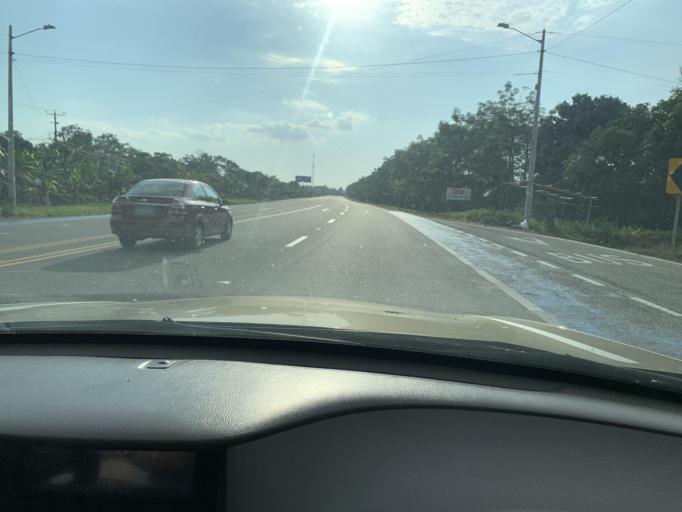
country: EC
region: Guayas
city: Coronel Marcelino Mariduena
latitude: -2.2797
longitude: -79.5231
